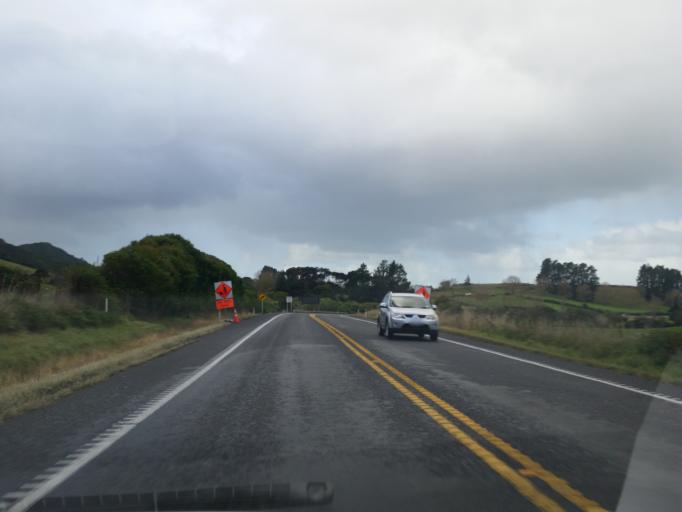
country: NZ
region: Auckland
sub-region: Auckland
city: Pukekohe East
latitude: -37.2122
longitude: 175.0751
